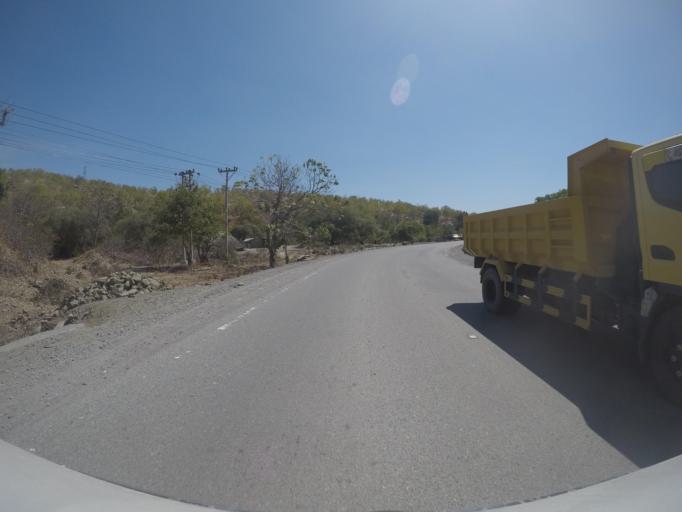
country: TL
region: Liquica
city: Liquica
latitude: -8.5686
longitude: 125.4351
